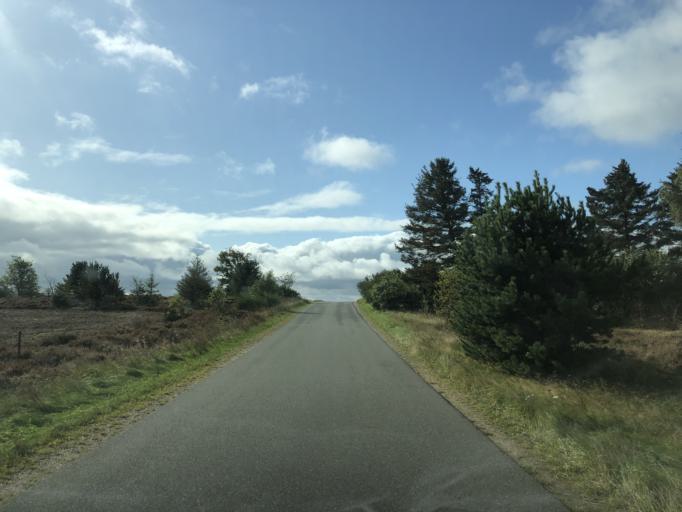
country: DK
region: Central Jutland
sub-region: Holstebro Kommune
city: Holstebro
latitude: 56.3203
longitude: 8.4683
